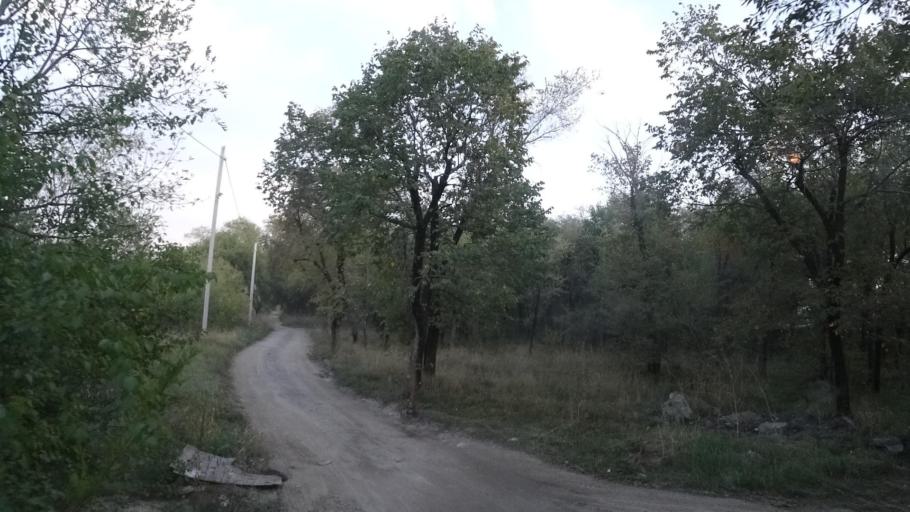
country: KZ
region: Almaty Oblysy
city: Pervomayskiy
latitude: 43.3368
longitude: 76.9980
